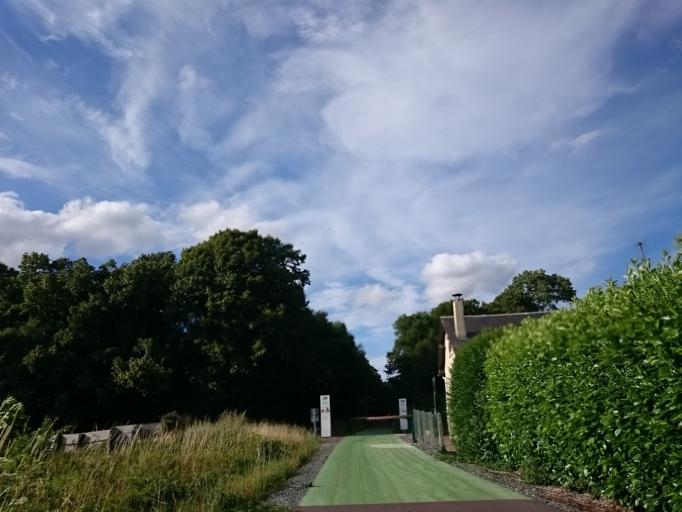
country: FR
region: Lower Normandy
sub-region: Departement du Calvados
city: Saint-Andre-sur-Orne
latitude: 49.1299
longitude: -0.4022
